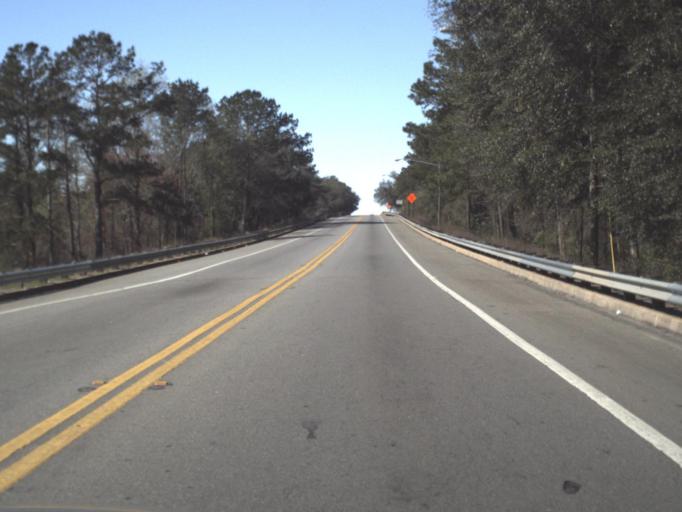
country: US
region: Florida
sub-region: Leon County
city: Tallahassee
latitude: 30.4390
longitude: -84.3439
